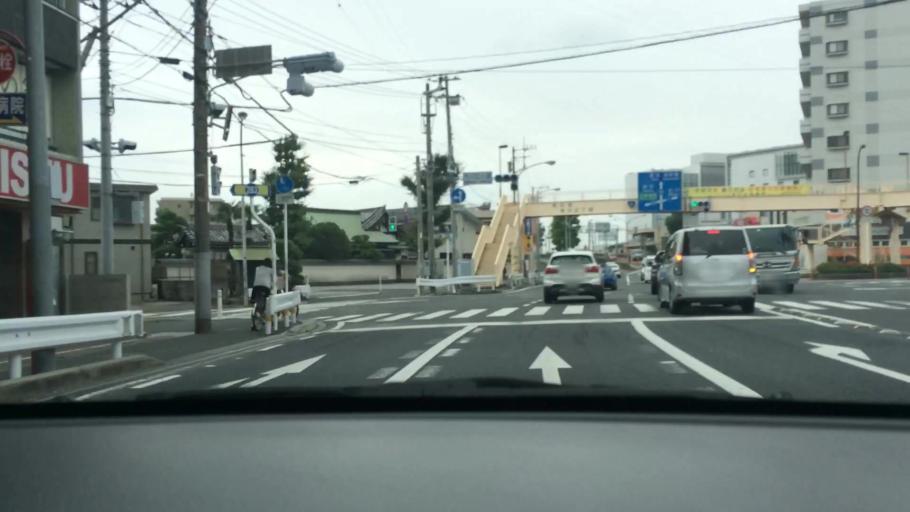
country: JP
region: Chiba
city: Matsudo
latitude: 35.7323
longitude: 139.9028
